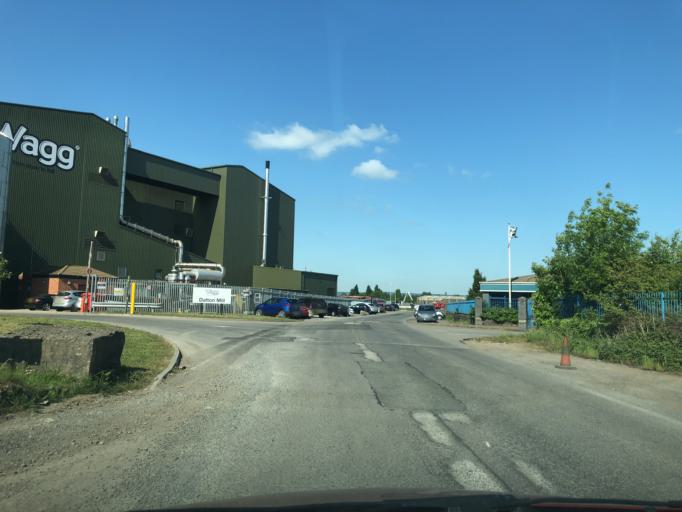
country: GB
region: England
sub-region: North Yorkshire
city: Thirsk
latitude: 54.1731
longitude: -1.3597
